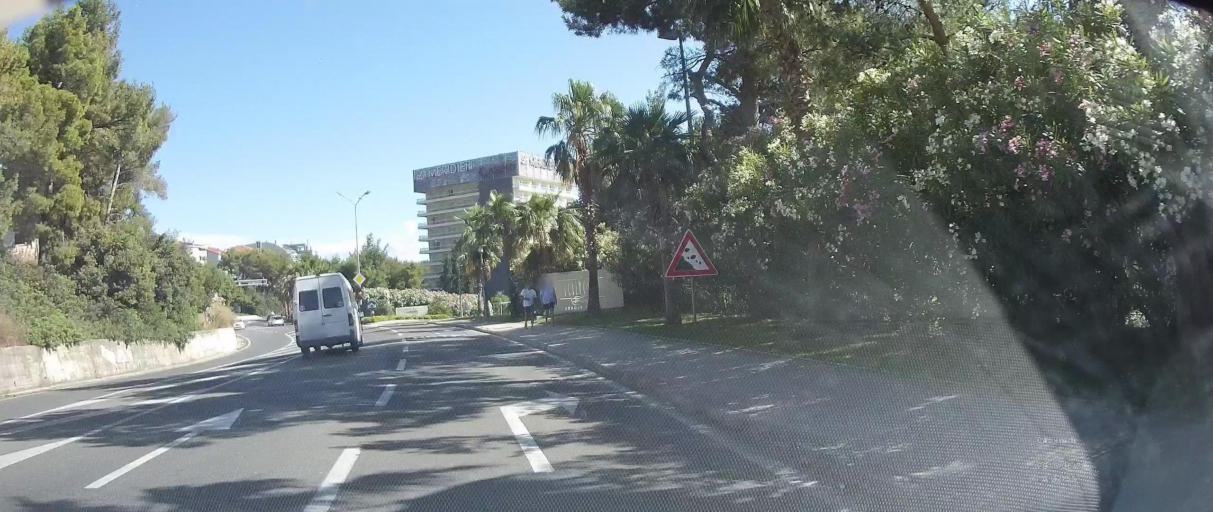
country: HR
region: Splitsko-Dalmatinska
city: Podstrana
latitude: 43.4943
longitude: 16.5387
